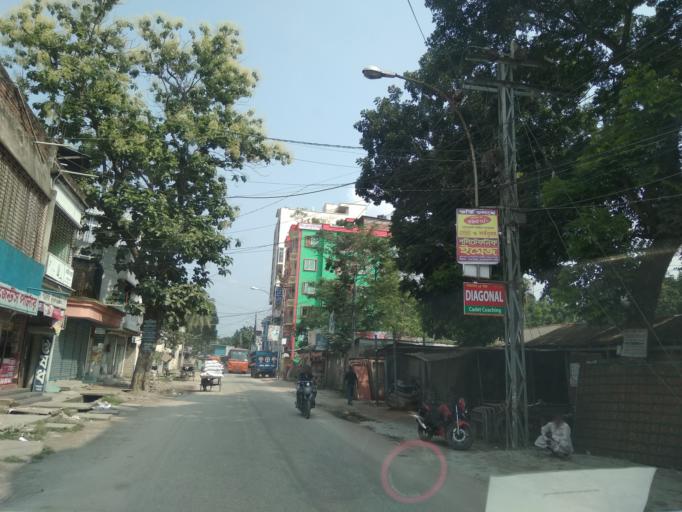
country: BD
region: Rangpur Division
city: Rangpur
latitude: 25.7602
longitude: 89.2321
